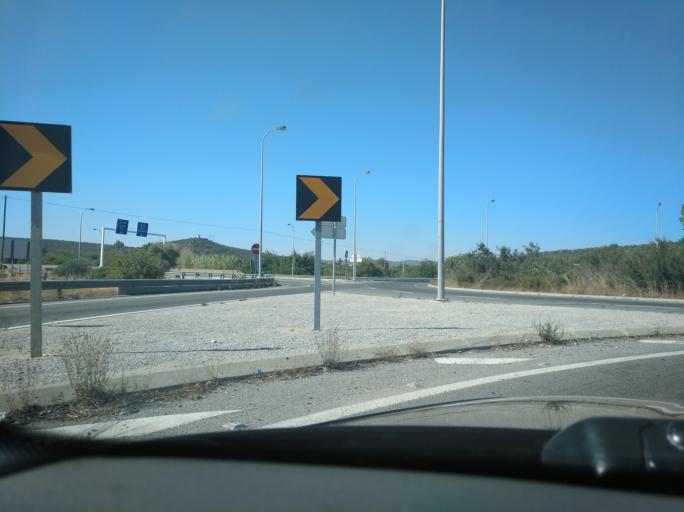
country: PT
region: Faro
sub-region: Olhao
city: Moncarapacho
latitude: 37.1071
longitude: -7.7978
